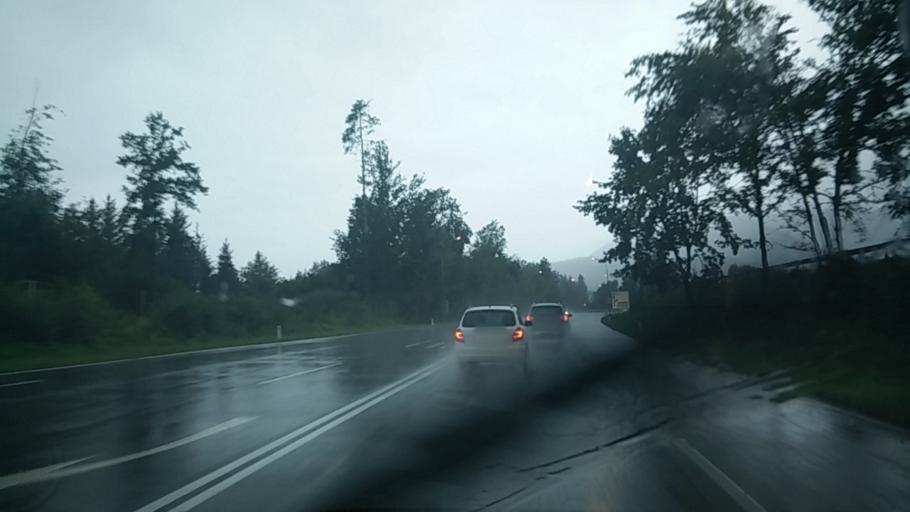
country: AT
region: Carinthia
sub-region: Politischer Bezirk Villach Land
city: Wernberg
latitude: 46.6230
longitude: 13.8962
